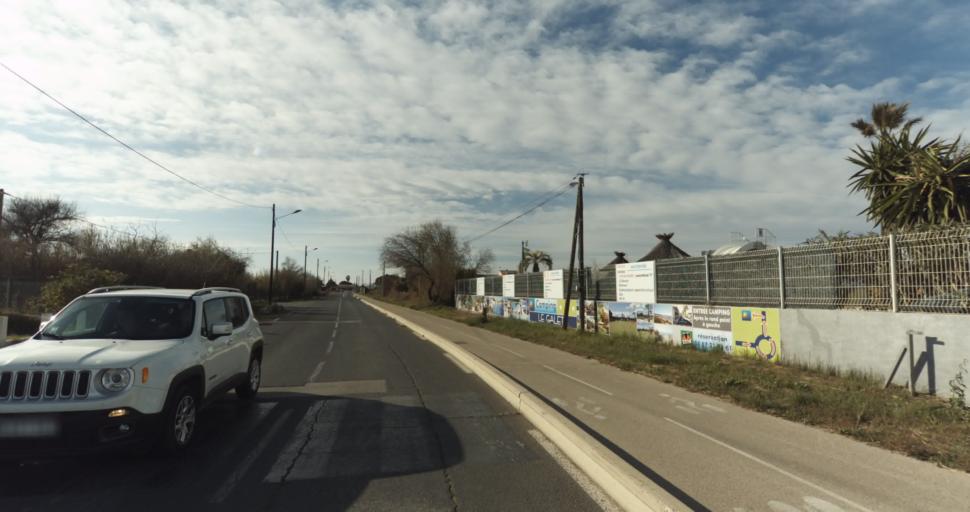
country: FR
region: Languedoc-Roussillon
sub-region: Departement de l'Herault
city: Le Cap d'Agde
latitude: 43.3134
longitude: 3.5397
